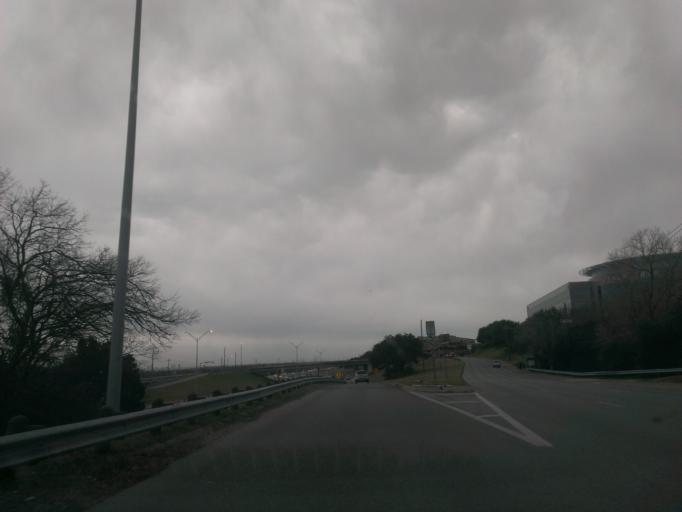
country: US
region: Texas
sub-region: Travis County
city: West Lake Hills
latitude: 30.3546
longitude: -97.7480
